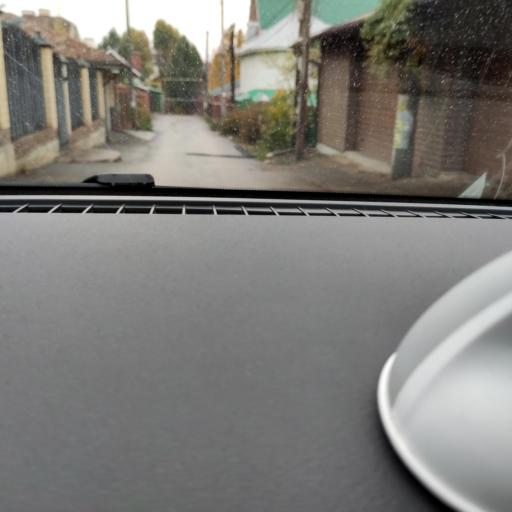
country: RU
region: Samara
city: Samara
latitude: 53.2690
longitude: 50.2125
